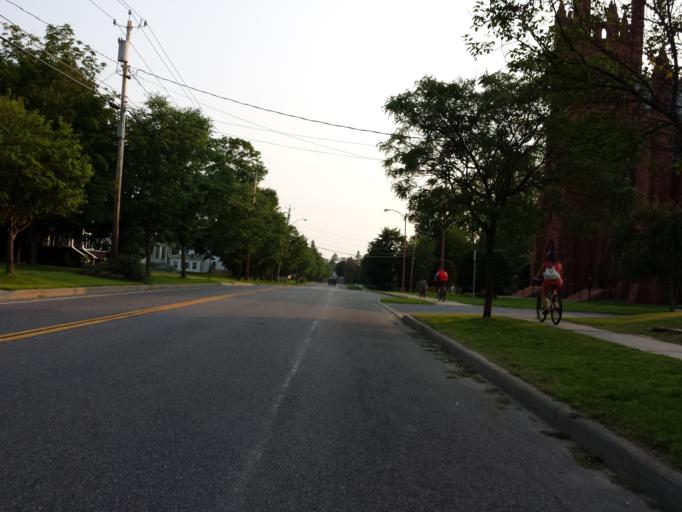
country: US
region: New York
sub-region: St. Lawrence County
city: Potsdam
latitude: 44.6731
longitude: -74.9774
